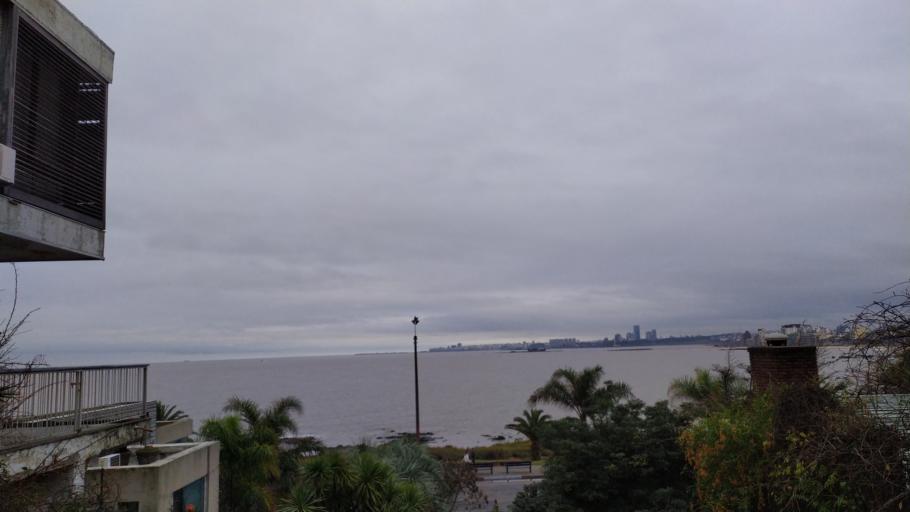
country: UY
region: Canelones
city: Paso de Carrasco
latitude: -34.8968
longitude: -56.0828
